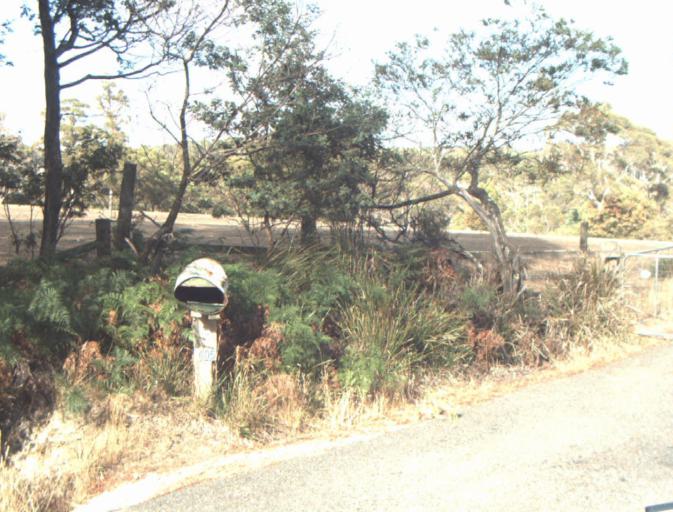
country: AU
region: Tasmania
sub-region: Dorset
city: Bridport
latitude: -41.1200
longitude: 147.2045
